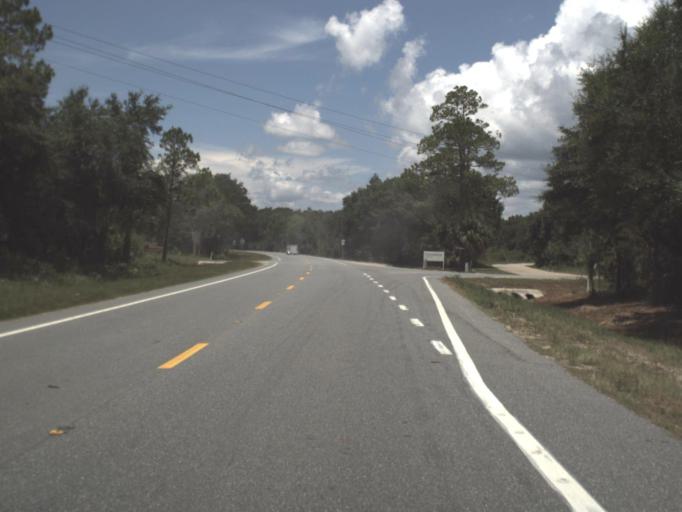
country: US
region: Florida
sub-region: Leon County
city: Woodville
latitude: 30.1441
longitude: -83.9436
